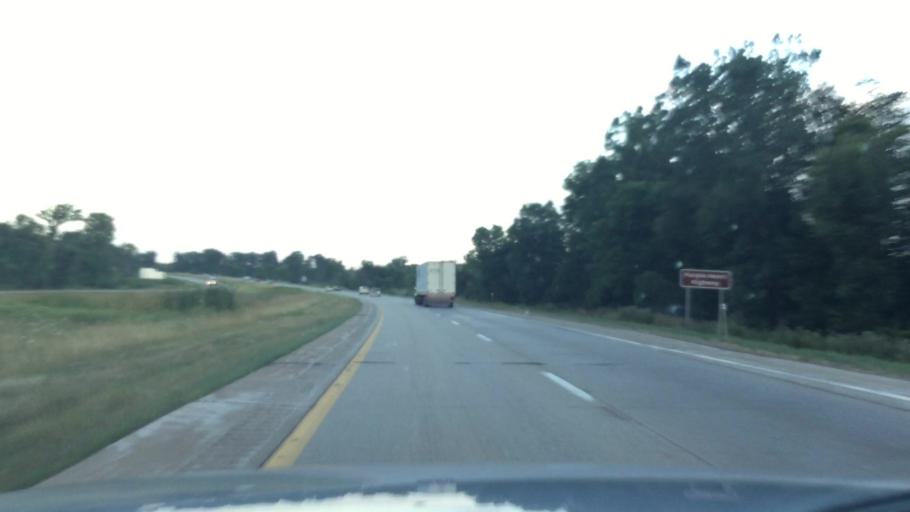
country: US
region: Michigan
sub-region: Shiawassee County
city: Perry
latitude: 42.8392
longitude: -84.2272
